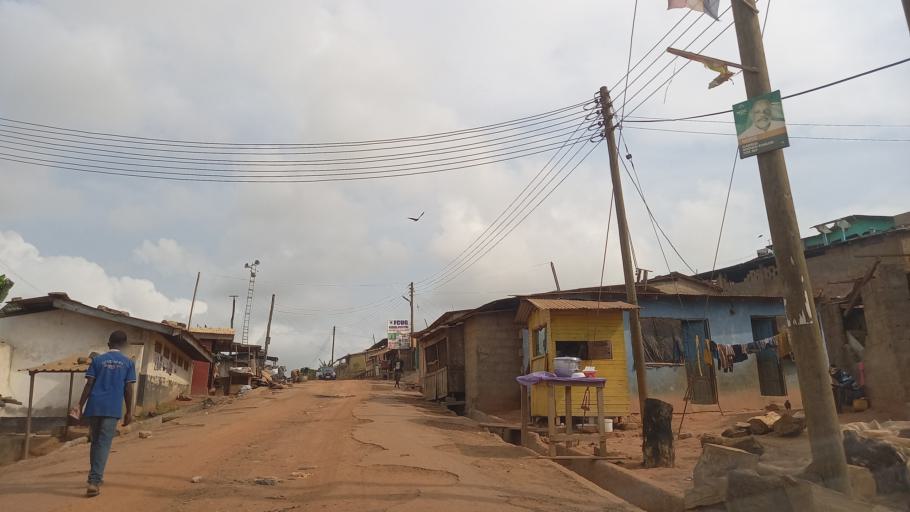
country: GH
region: Western
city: Shama Junction
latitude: 4.9840
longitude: -1.6376
